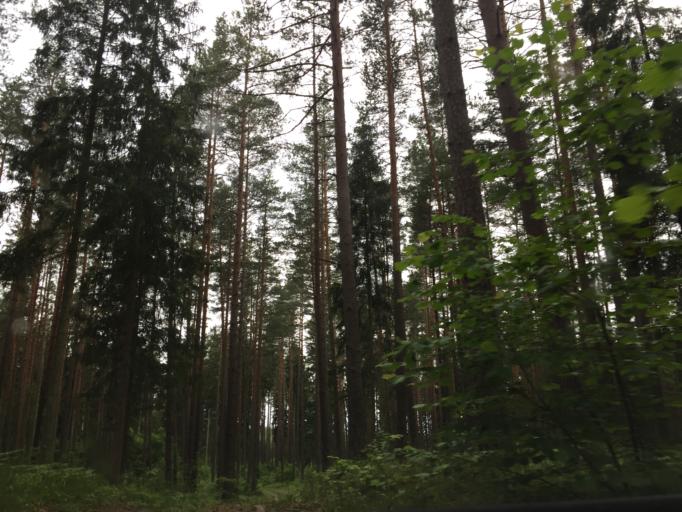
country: LV
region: Tukuma Rajons
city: Tukums
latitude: 57.0273
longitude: 23.0767
